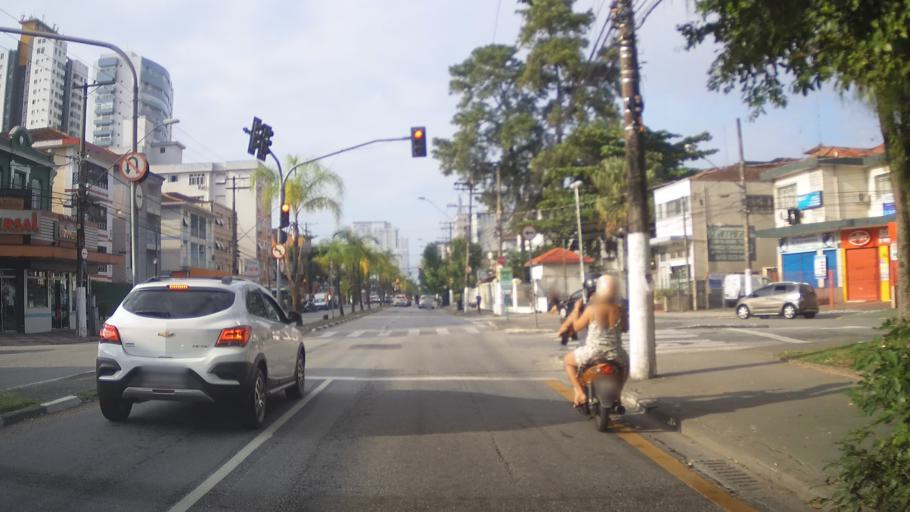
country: BR
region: Sao Paulo
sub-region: Santos
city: Santos
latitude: -23.9545
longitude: -46.3226
